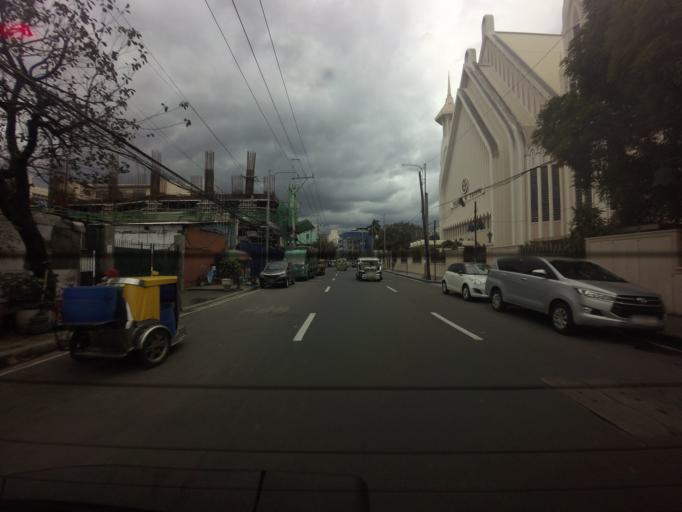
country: PH
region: Metro Manila
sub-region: City of Manila
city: Manila
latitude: 14.6108
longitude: 120.9694
